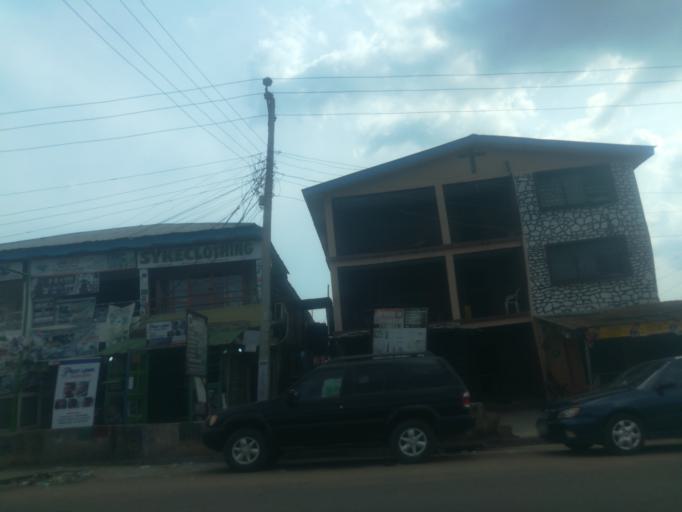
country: NG
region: Ogun
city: Abeokuta
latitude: 7.1358
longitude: 3.3302
